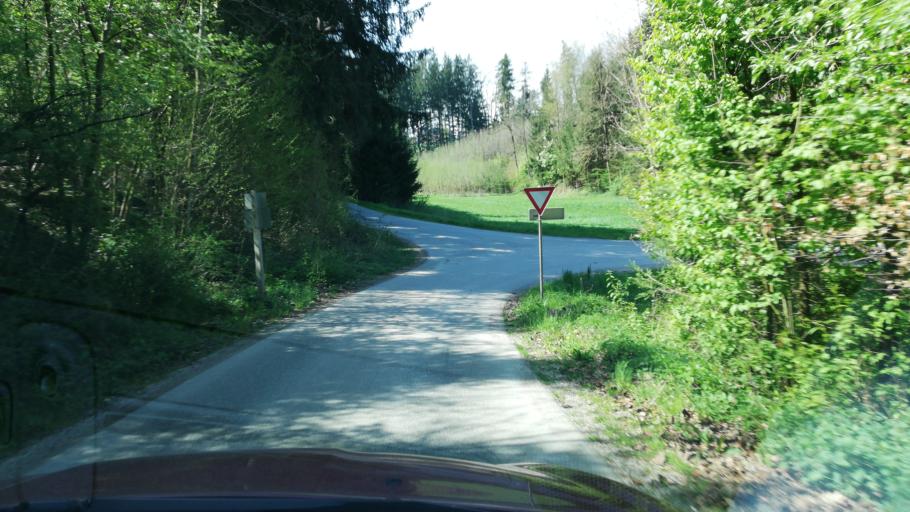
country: AT
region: Upper Austria
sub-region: Politischer Bezirk Kirchdorf an der Krems
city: Kremsmunster
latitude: 48.0410
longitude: 14.1594
